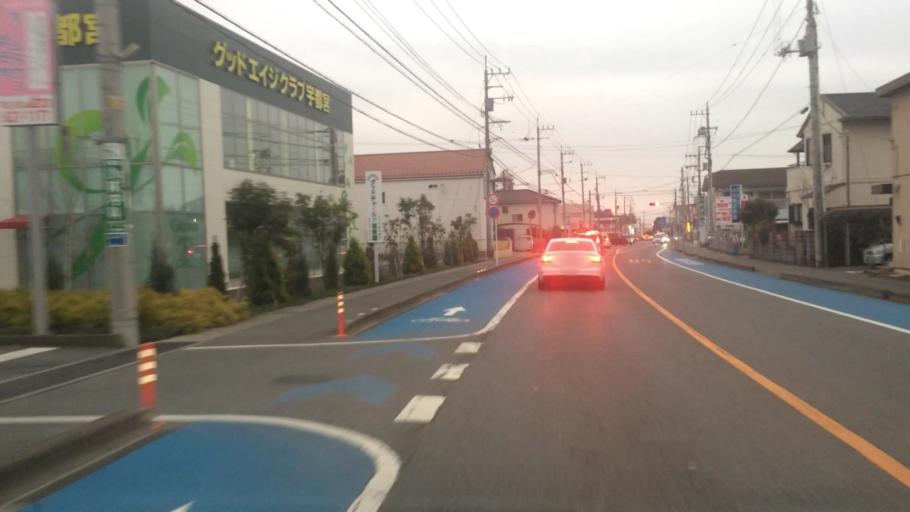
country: JP
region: Tochigi
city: Utsunomiya-shi
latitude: 36.5937
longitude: 139.8536
